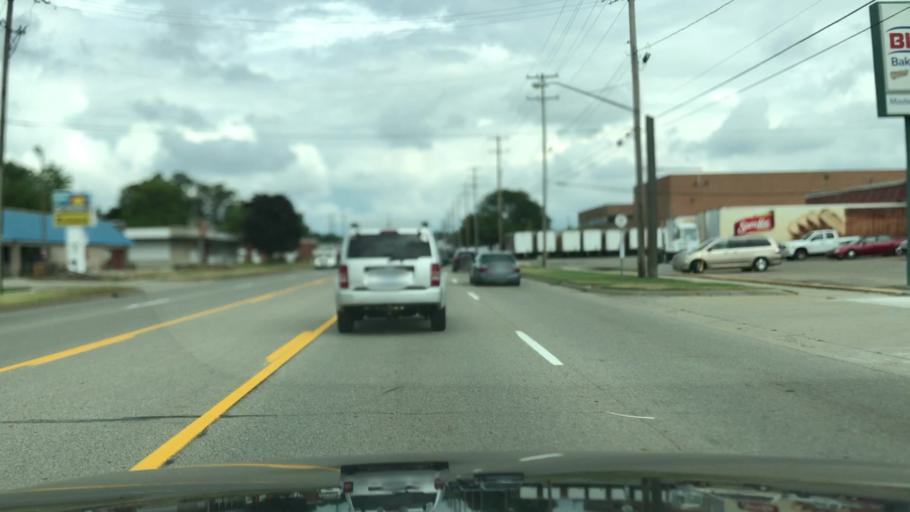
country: US
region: Michigan
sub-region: Kent County
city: Wyoming
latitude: 42.9129
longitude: -85.6620
